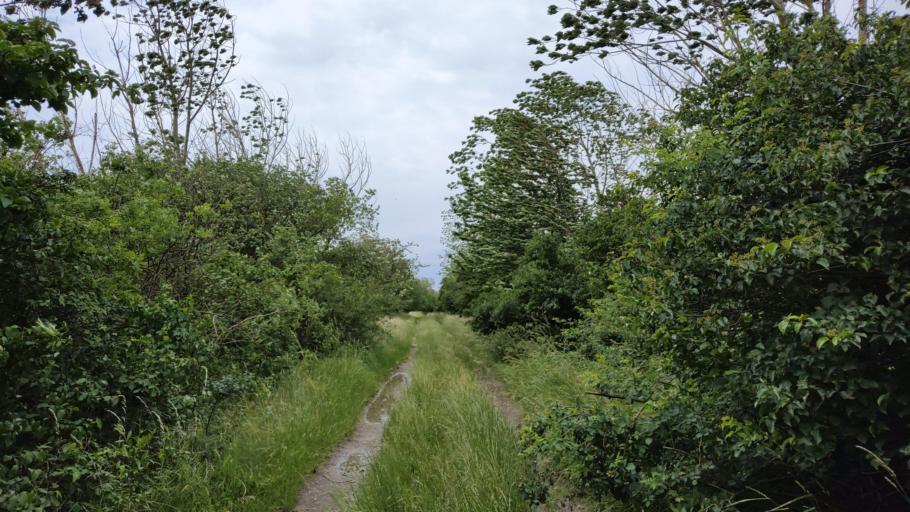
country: HU
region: Vas
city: Szombathely
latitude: 47.2605
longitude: 16.6425
